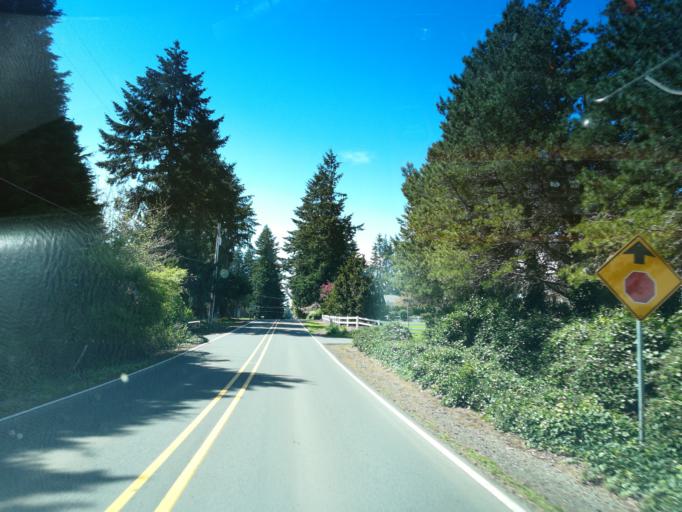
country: US
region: Oregon
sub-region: Clackamas County
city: Damascus
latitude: 45.4325
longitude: -122.4319
